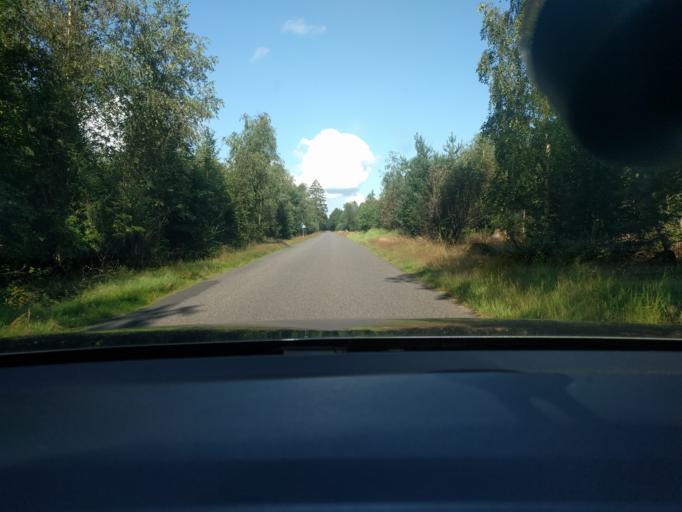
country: DK
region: Central Jutland
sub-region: Viborg Kommune
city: Viborg
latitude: 56.4137
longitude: 9.3544
